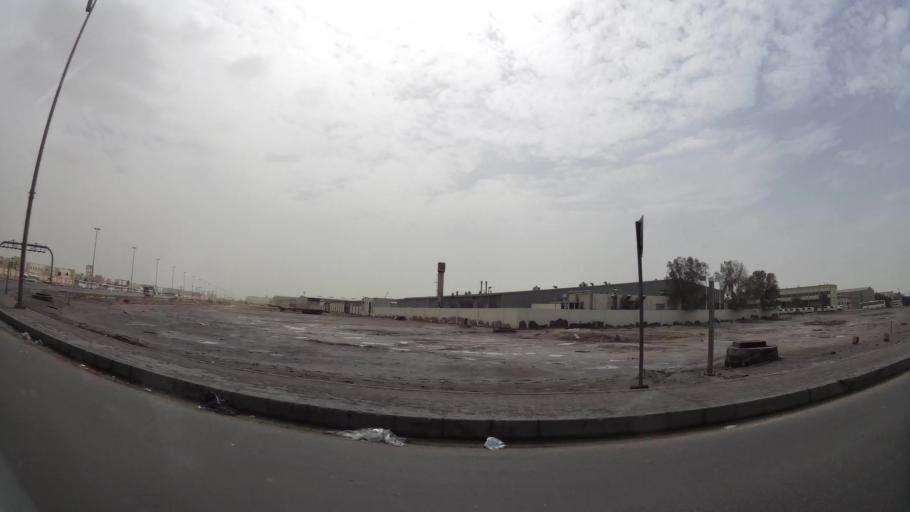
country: AE
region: Abu Dhabi
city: Abu Dhabi
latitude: 24.3447
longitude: 54.4823
